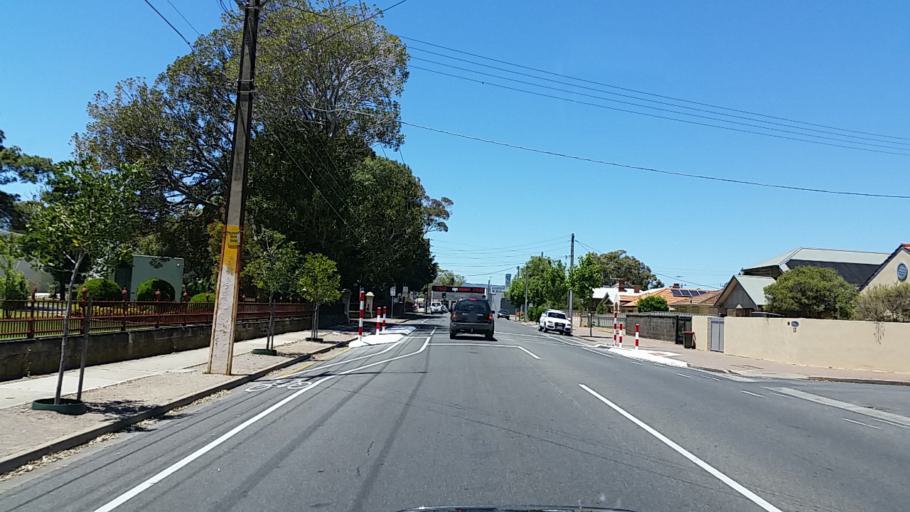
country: AU
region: South Australia
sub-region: Holdfast Bay
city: North Brighton
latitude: -34.9967
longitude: 138.5197
